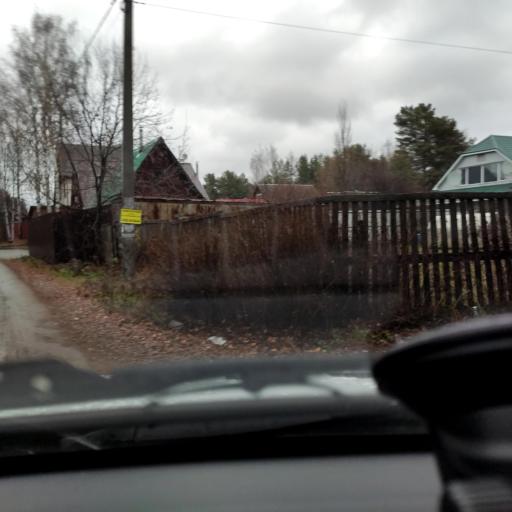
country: RU
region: Perm
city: Perm
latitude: 58.0607
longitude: 56.3046
